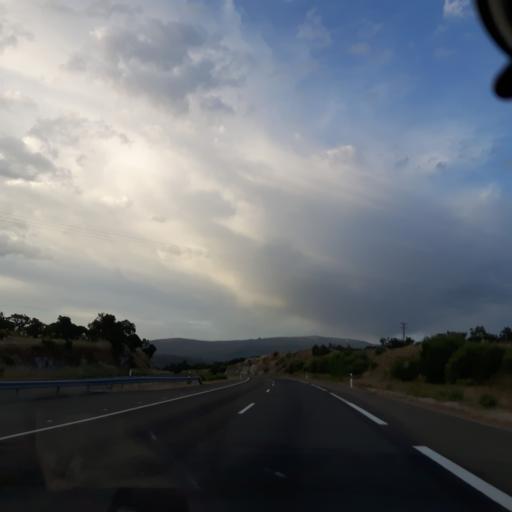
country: ES
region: Castille and Leon
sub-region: Provincia de Salamanca
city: Nava de Bejar
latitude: 40.4738
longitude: -5.6822
